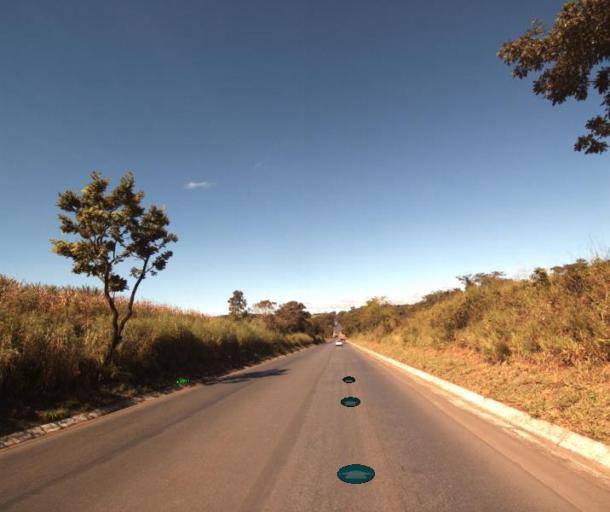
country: BR
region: Goias
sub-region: Itapaci
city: Itapaci
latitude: -14.9982
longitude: -49.4098
